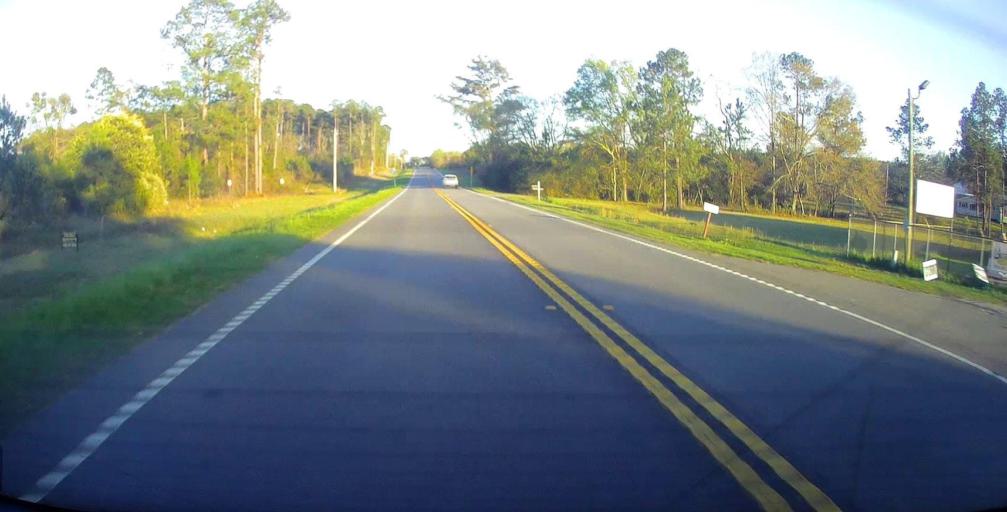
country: US
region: Georgia
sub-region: Crisp County
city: Cordele
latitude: 31.9546
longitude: -83.7252
